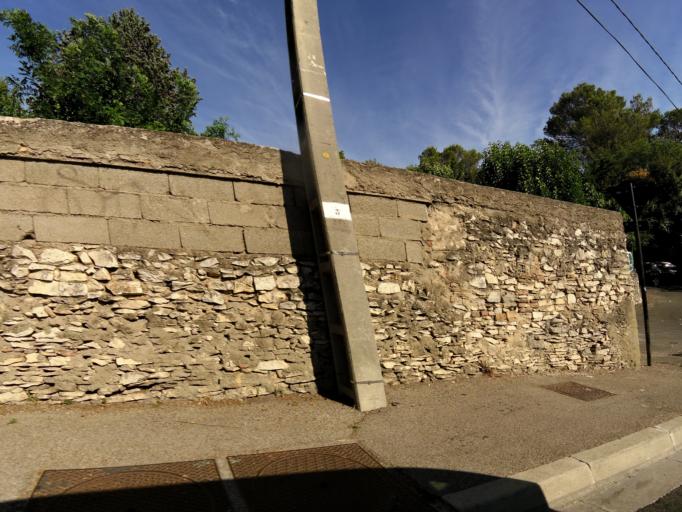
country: FR
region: Languedoc-Roussillon
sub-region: Departement du Gard
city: Nimes
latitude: 43.8417
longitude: 4.3414
